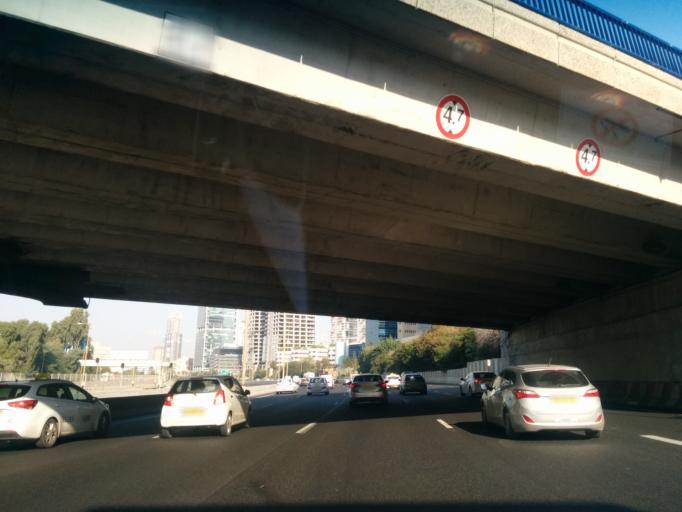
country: IL
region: Tel Aviv
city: Tel Aviv
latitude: 32.0645
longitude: 34.7902
